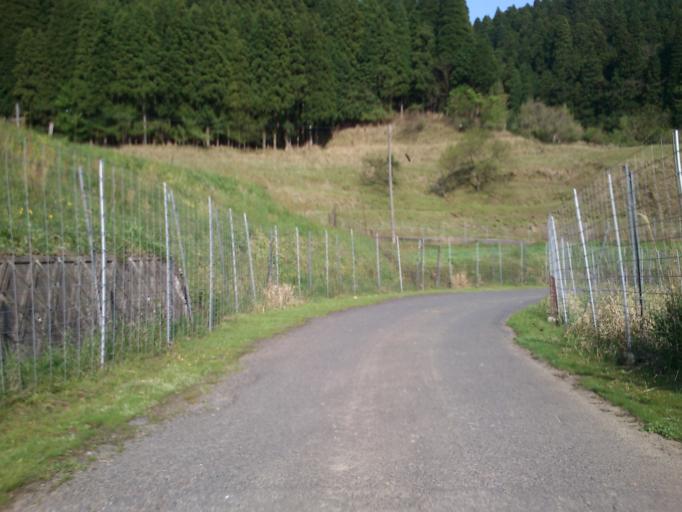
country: JP
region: Kyoto
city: Fukuchiyama
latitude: 35.3805
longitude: 135.0103
